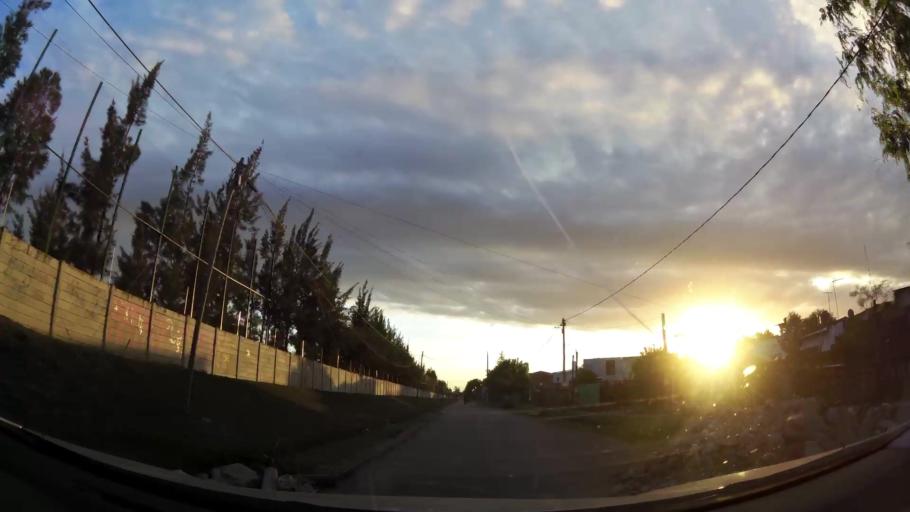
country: AR
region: Buenos Aires
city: Santa Catalina - Dique Lujan
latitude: -34.4340
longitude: -58.6631
